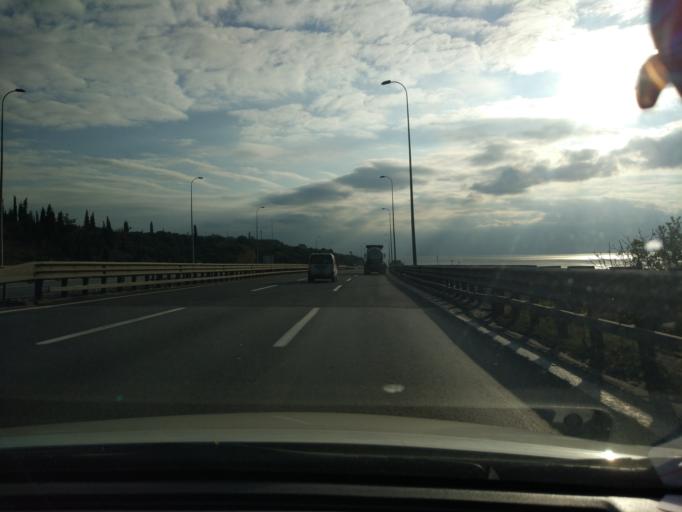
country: TR
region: Kocaeli
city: Tavsancil
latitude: 40.7727
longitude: 29.5591
